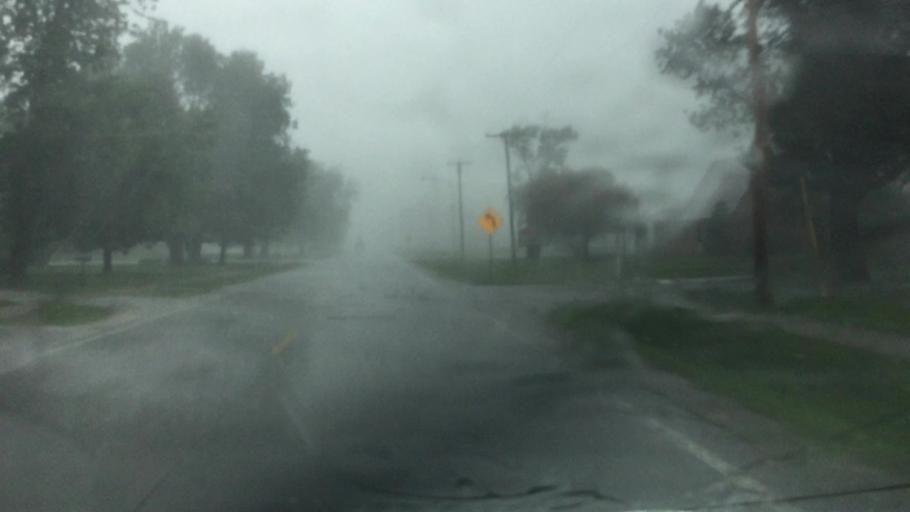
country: US
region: Illinois
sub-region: Hancock County
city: Carthage
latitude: 40.2354
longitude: -91.0645
